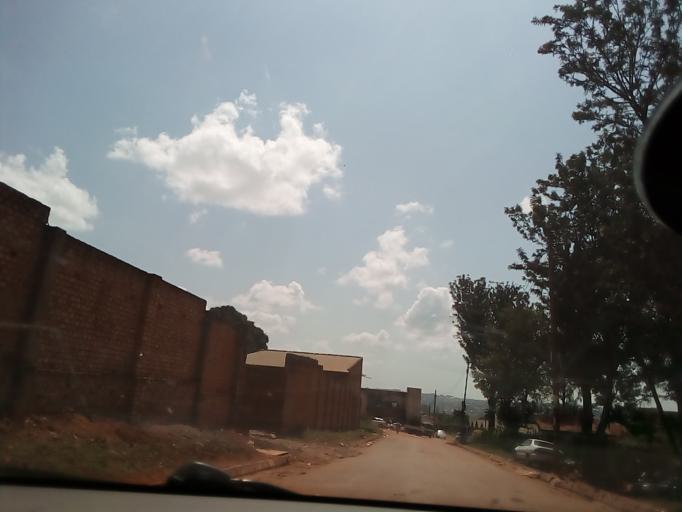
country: UG
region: Central Region
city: Masaka
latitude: -0.3390
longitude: 31.7396
